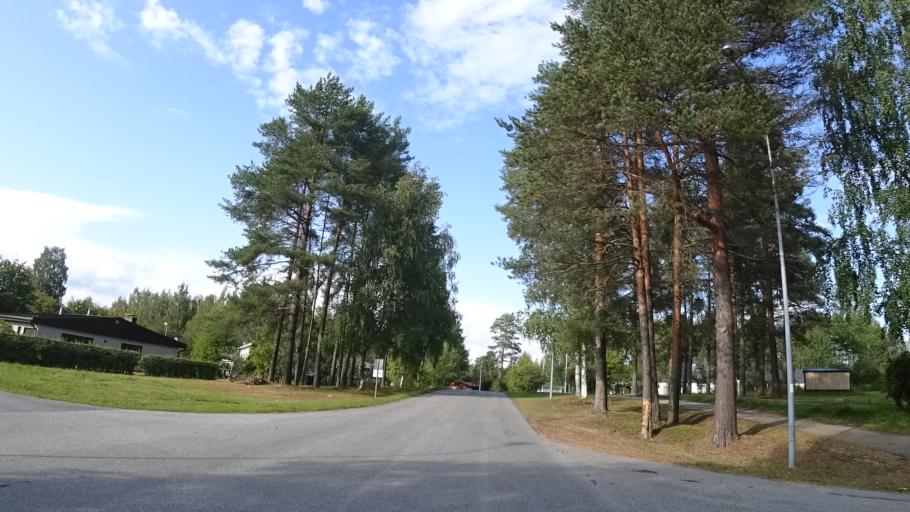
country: FI
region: North Karelia
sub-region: Pielisen Karjala
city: Lieksa
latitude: 63.3315
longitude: 30.0292
